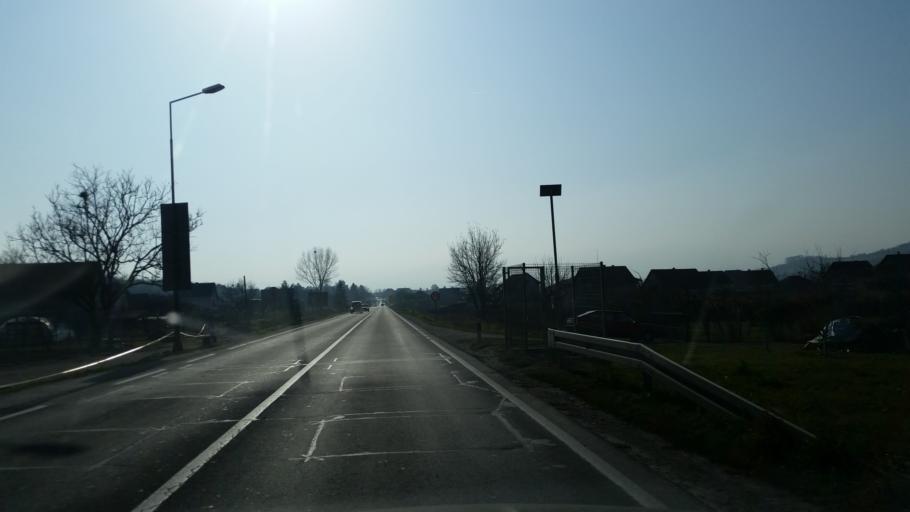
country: RS
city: Prislonica
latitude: 43.9246
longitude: 20.4094
